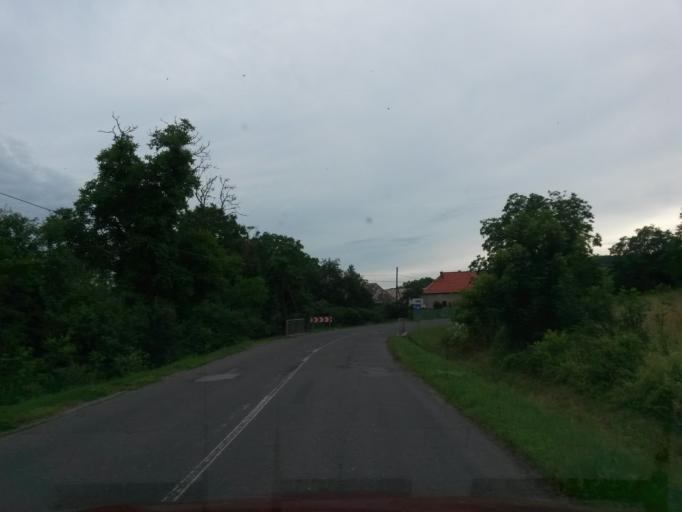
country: SK
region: Banskobystricky
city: Velky Krtis
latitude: 48.3129
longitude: 19.3998
